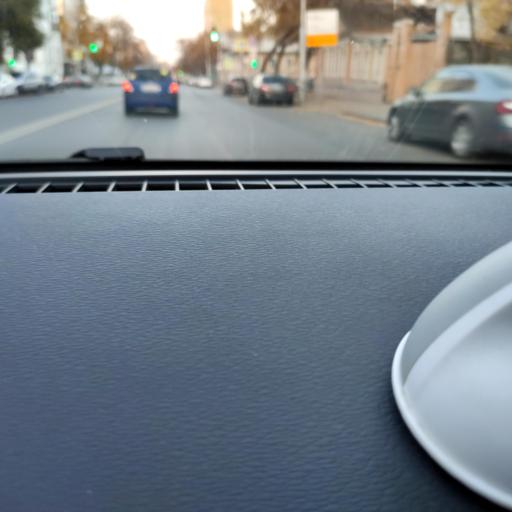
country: RU
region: Samara
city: Samara
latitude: 53.2016
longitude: 50.1159
